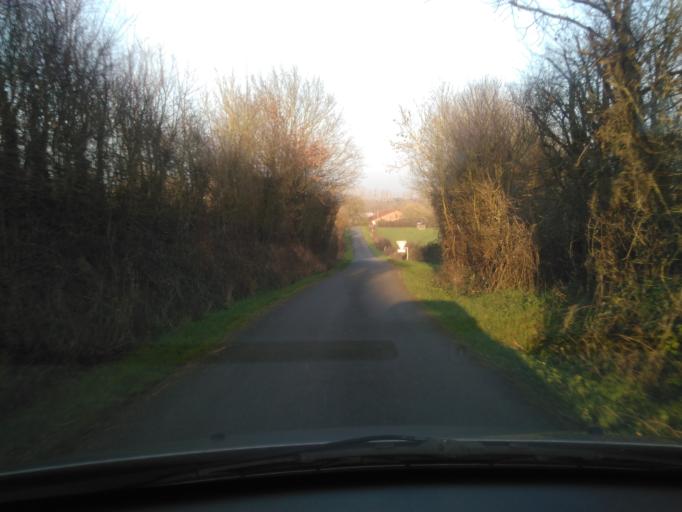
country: FR
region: Pays de la Loire
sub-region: Departement de la Vendee
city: Chantonnay
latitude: 46.6633
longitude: -1.0068
